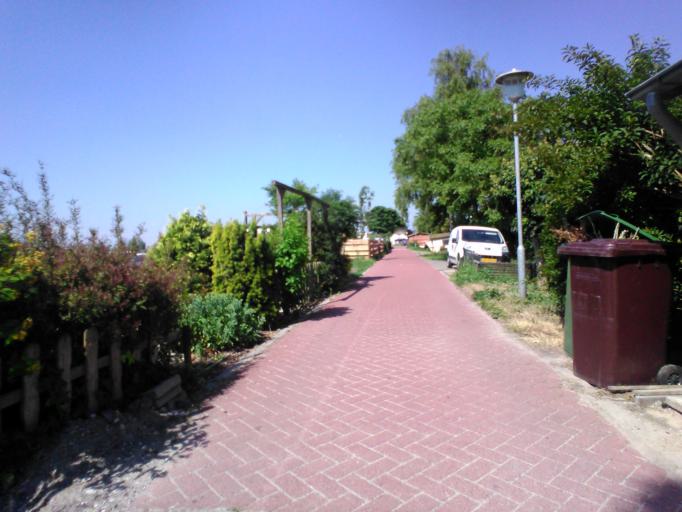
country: NL
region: South Holland
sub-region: Gemeente Boskoop
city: Boskoop
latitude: 52.0864
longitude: 4.6536
